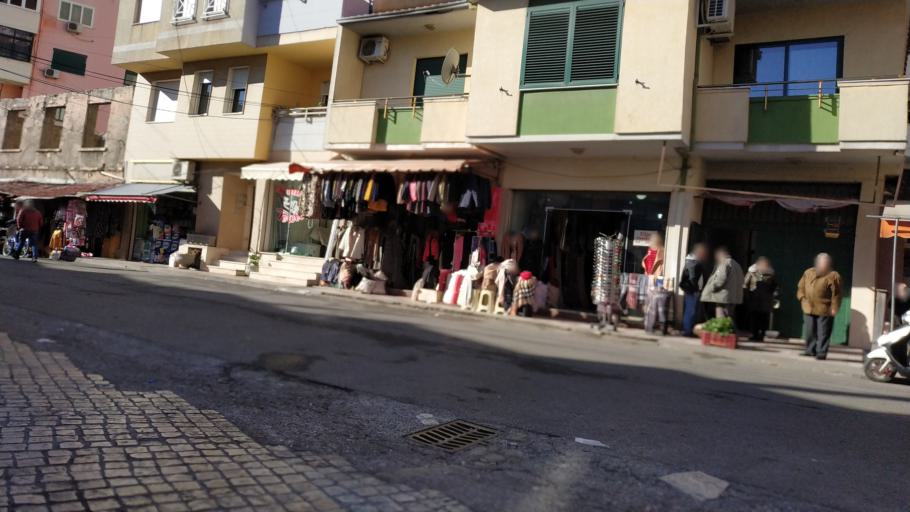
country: AL
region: Shkoder
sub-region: Rrethi i Shkodres
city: Shkoder
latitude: 42.0695
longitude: 19.5085
